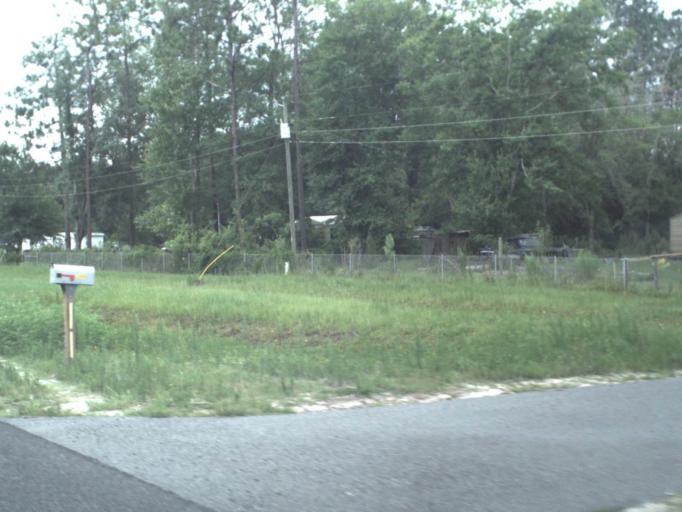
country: US
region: Florida
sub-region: Nassau County
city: Nassau Village-Ratliff
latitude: 30.4560
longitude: -81.9138
